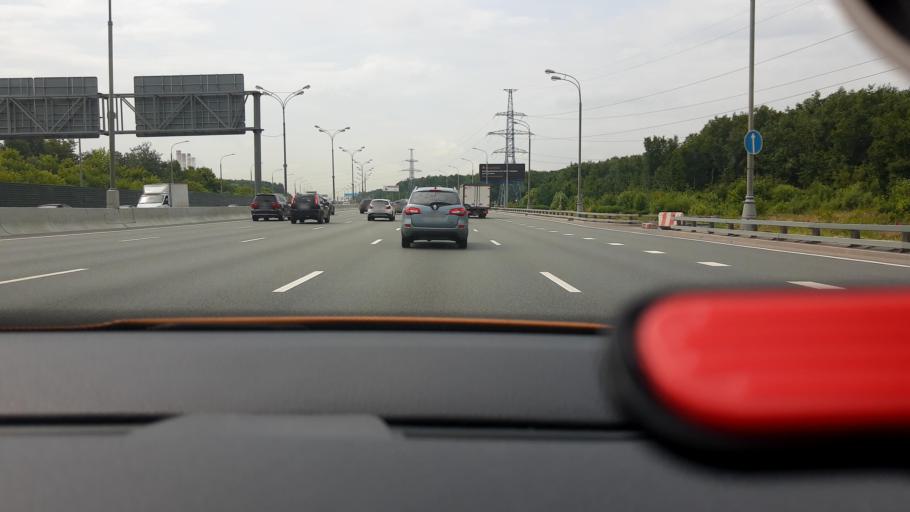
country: RU
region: Moscow
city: Vagonoremont
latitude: 55.9061
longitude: 37.5283
